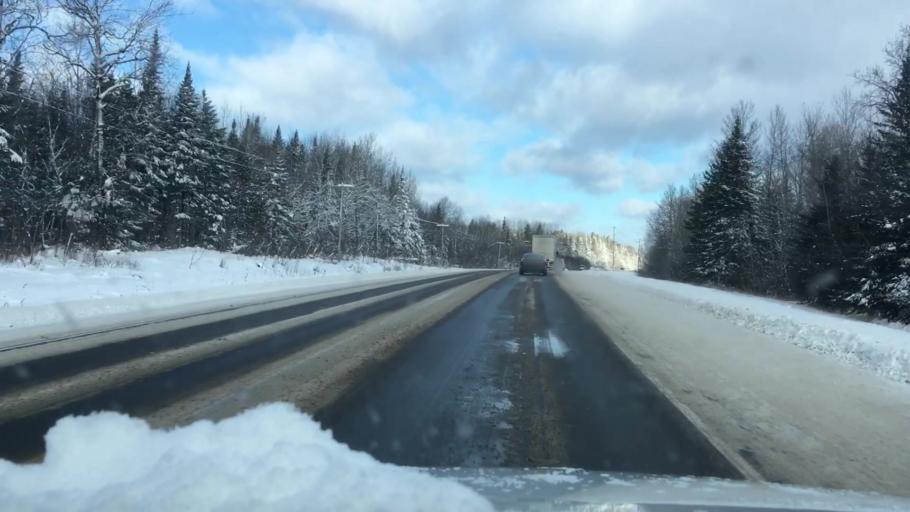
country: US
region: Maine
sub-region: Aroostook County
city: Caribou
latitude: 46.8367
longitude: -67.9995
